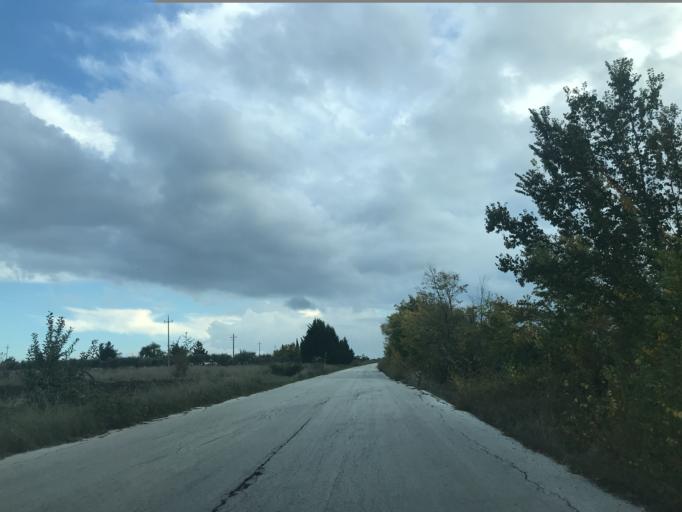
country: IT
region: Molise
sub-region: Provincia di Isernia
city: Bagnoli del Trigno
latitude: 41.6923
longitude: 14.4621
